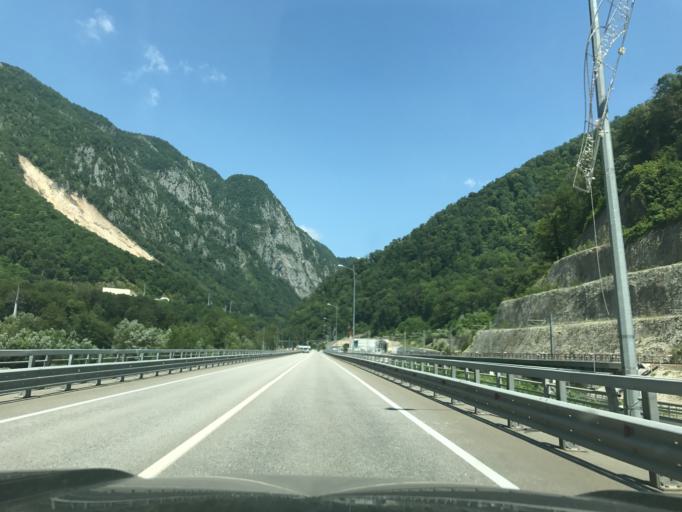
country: RU
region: Krasnodarskiy
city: Vysokoye
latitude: 43.5854
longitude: 40.0121
